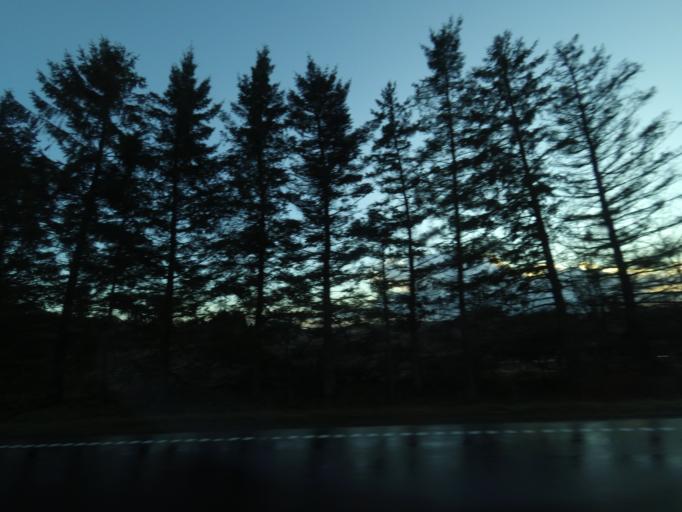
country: DK
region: Central Jutland
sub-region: Ikast-Brande Kommune
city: Brande
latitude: 56.0110
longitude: 9.0494
